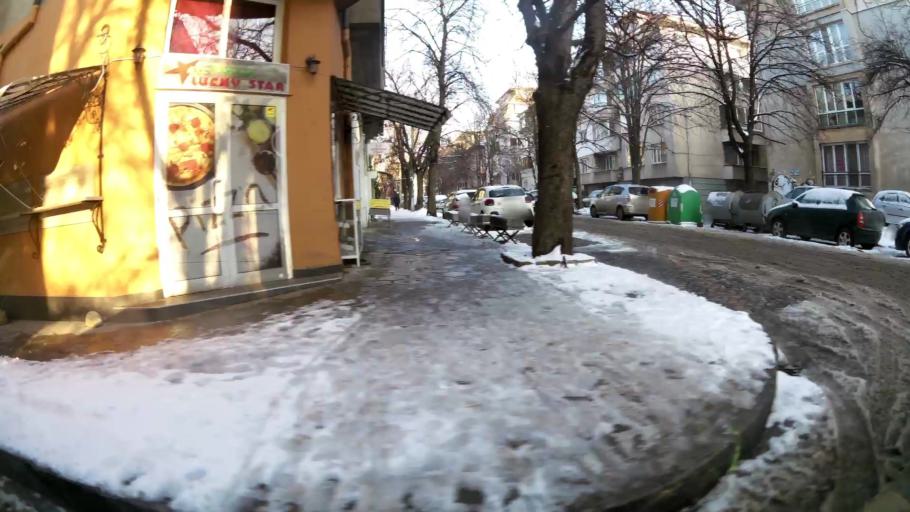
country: BG
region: Sofia-Capital
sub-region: Stolichna Obshtina
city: Sofia
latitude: 42.6846
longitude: 23.3547
